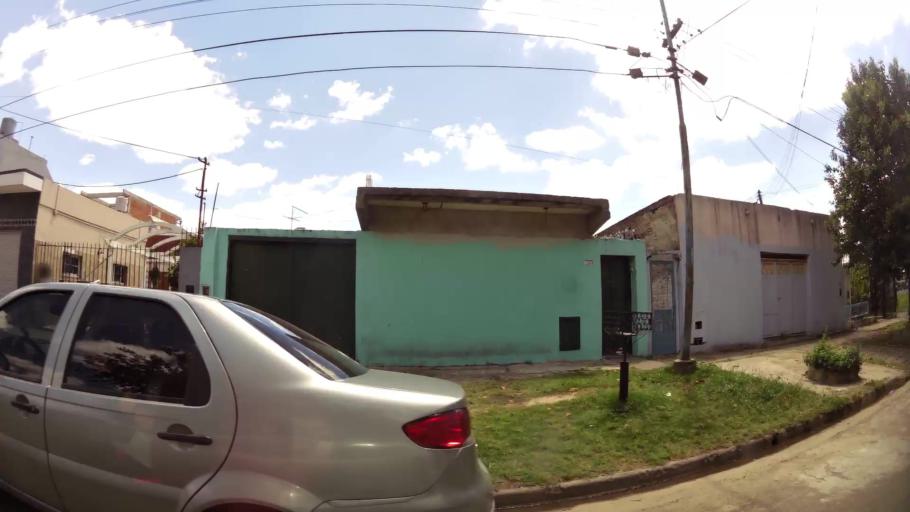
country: AR
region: Buenos Aires
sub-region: Partido de Lanus
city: Lanus
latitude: -34.7142
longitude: -58.4195
